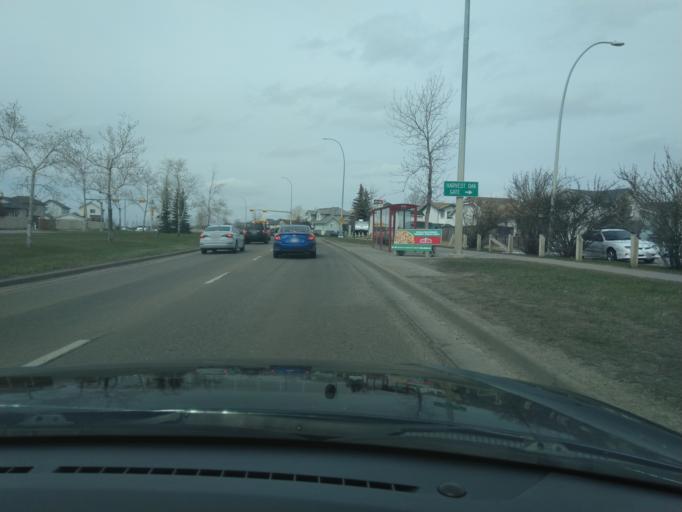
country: CA
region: Alberta
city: Calgary
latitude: 51.1460
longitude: -114.0643
